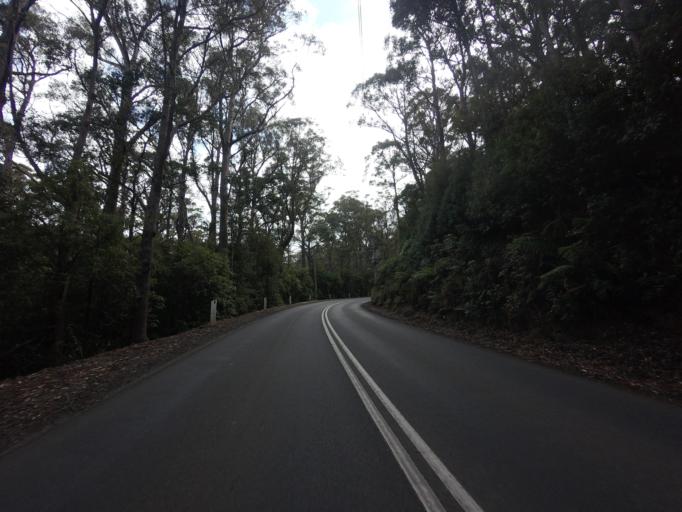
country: AU
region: Tasmania
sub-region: Hobart
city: Dynnyrne
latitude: -42.9211
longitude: 147.2639
